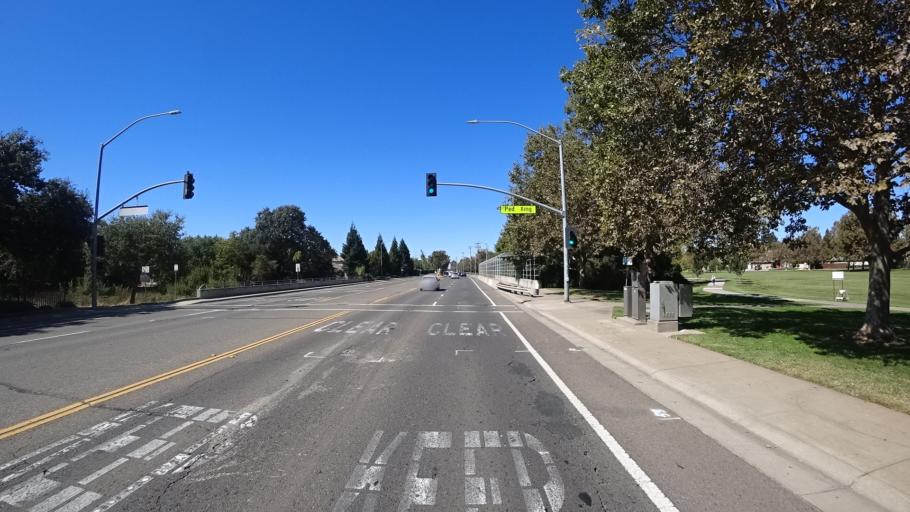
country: US
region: California
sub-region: Sacramento County
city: Elk Grove
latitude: 38.4236
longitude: -121.3739
